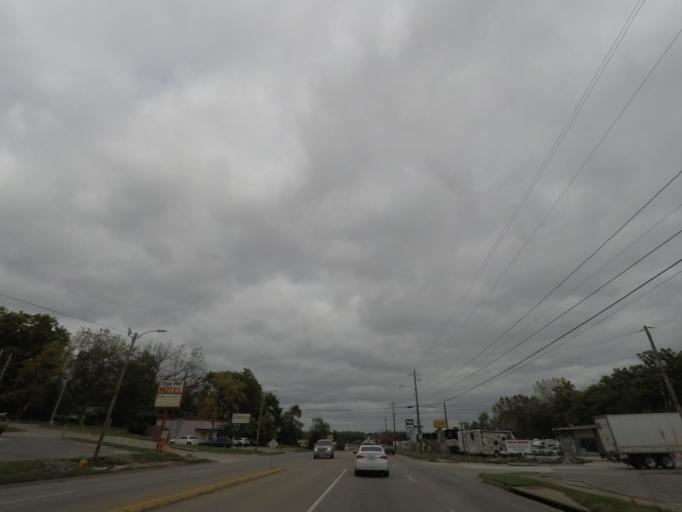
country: US
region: Iowa
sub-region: Polk County
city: Des Moines
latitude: 41.5658
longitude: -93.5968
